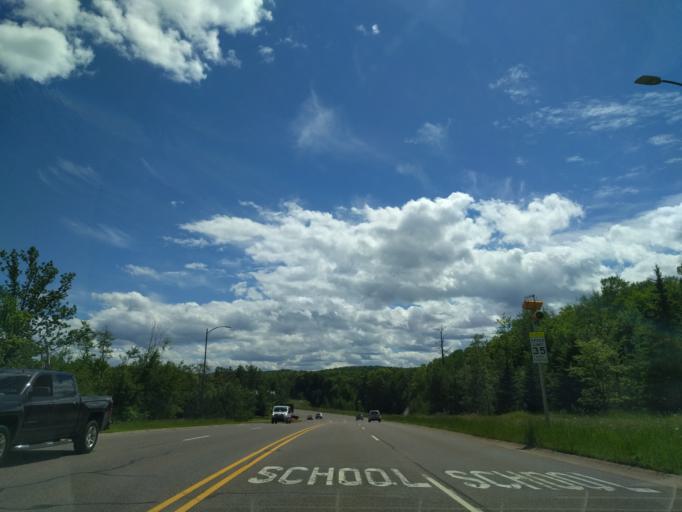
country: US
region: Michigan
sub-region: Marquette County
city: Marquette
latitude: 46.5348
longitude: -87.4174
